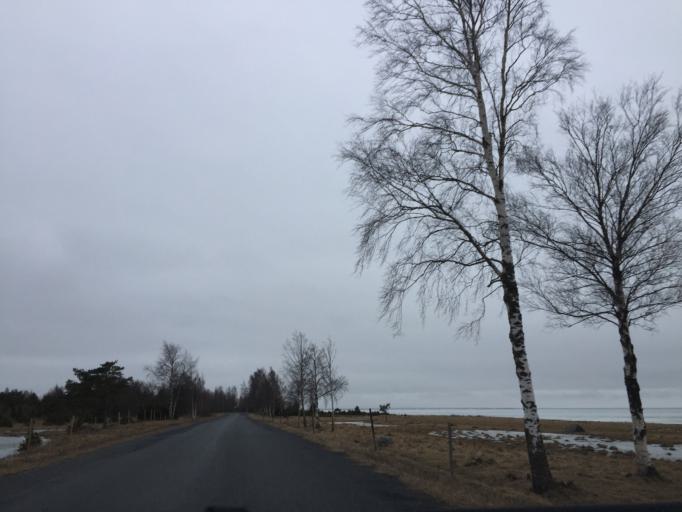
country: EE
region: Laeaene
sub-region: Haapsalu linn
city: Haapsalu
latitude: 58.7785
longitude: 23.4637
